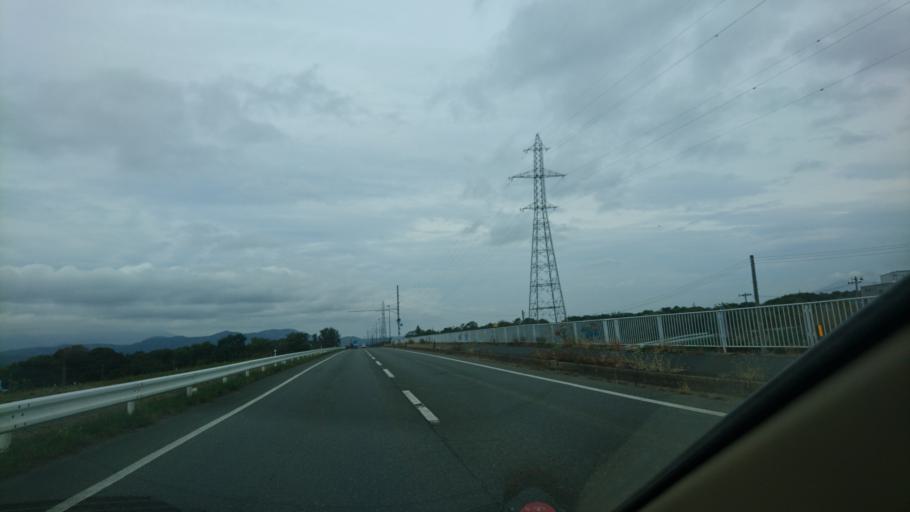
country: JP
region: Iwate
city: Morioka-shi
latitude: 39.7028
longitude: 141.1021
